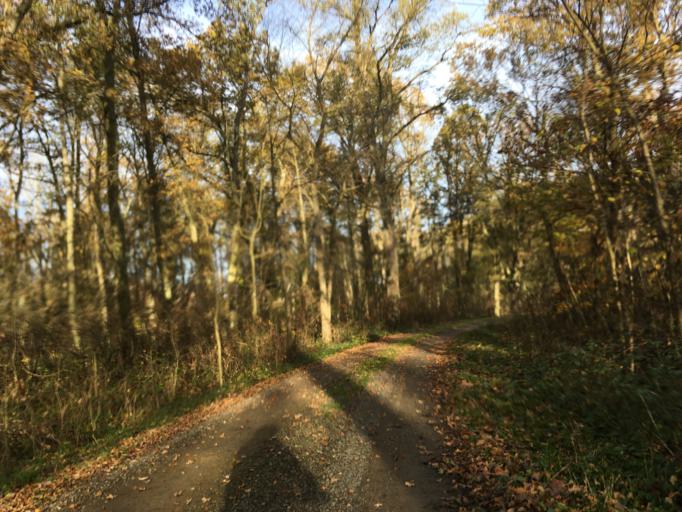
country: DE
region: Brandenburg
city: Schlepzig
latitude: 52.0020
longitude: 13.8629
